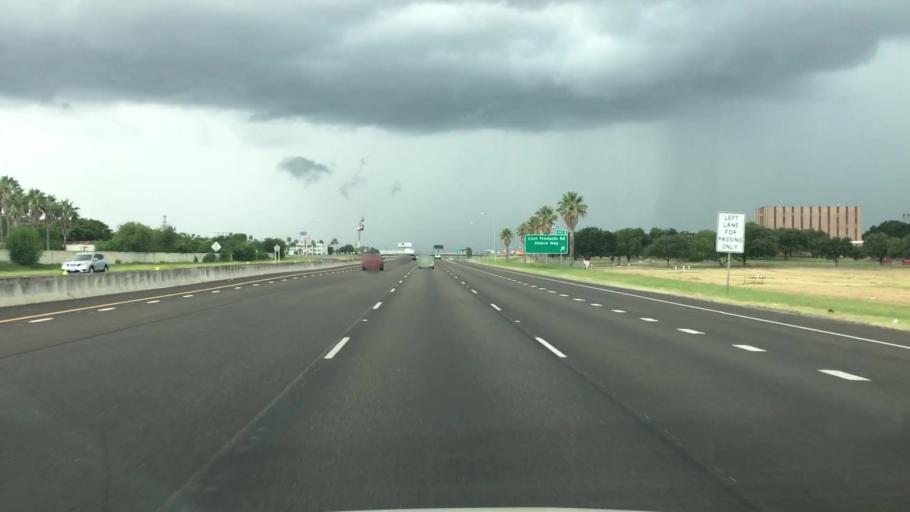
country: US
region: Texas
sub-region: Nueces County
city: Corpus Christi
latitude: 27.8047
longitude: -97.4787
